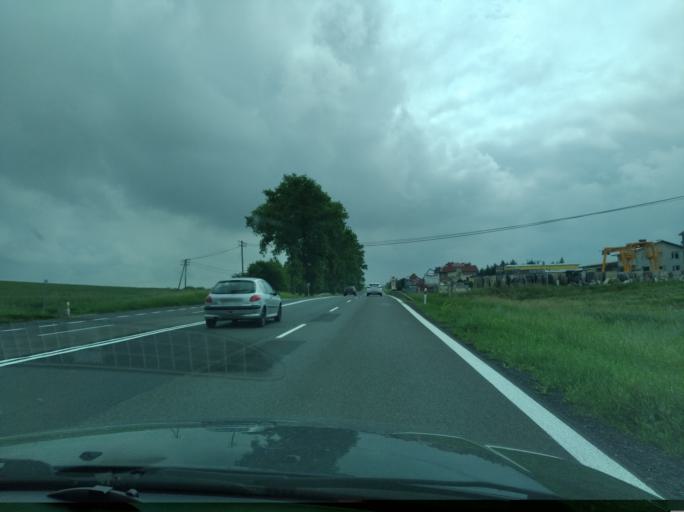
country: PL
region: Subcarpathian Voivodeship
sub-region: Powiat przeworski
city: Rozborz
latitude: 50.0516
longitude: 22.5228
